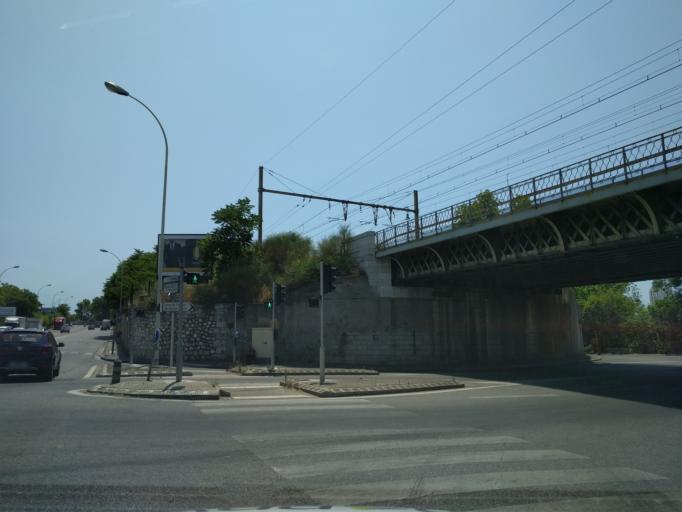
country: FR
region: Provence-Alpes-Cote d'Azur
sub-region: Departement des Bouches-du-Rhone
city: Marseille 14
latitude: 43.3481
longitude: 5.3623
